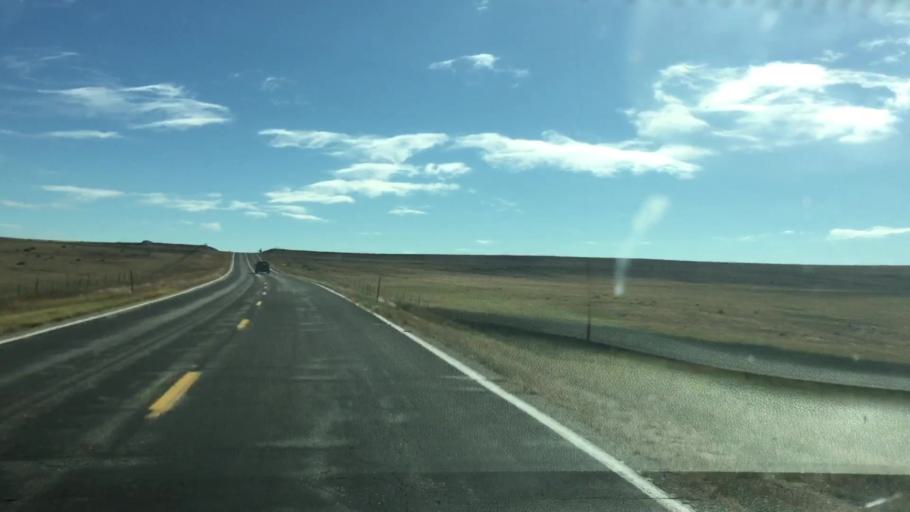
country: US
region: Colorado
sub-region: Elbert County
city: Kiowa
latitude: 39.2737
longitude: -104.2476
